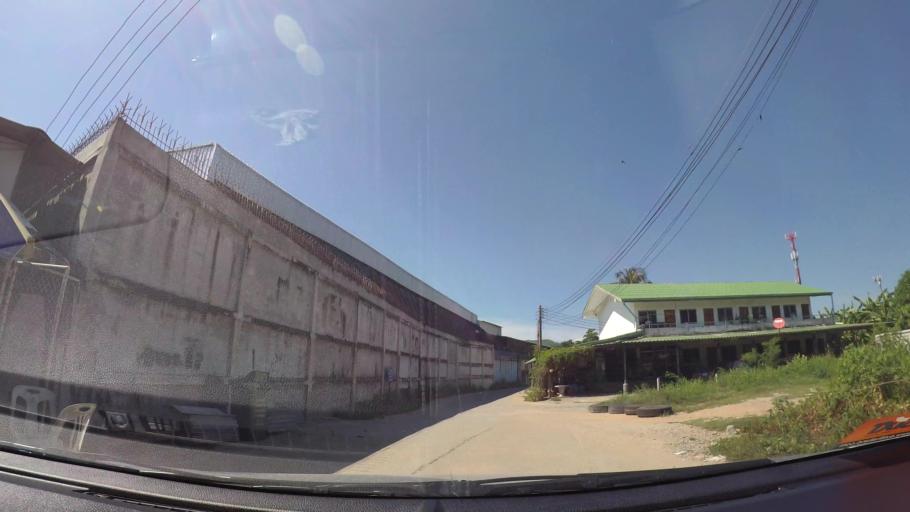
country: TH
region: Chon Buri
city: Si Racha
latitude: 13.1627
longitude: 100.9348
